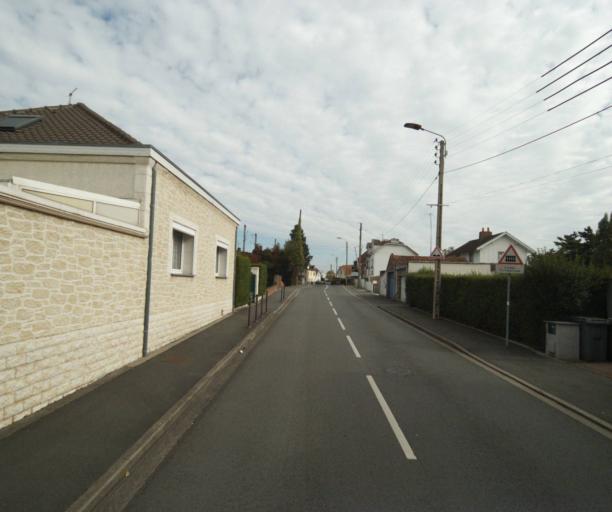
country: FR
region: Nord-Pas-de-Calais
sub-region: Departement du Nord
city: Templemars
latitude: 50.5755
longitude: 3.0488
